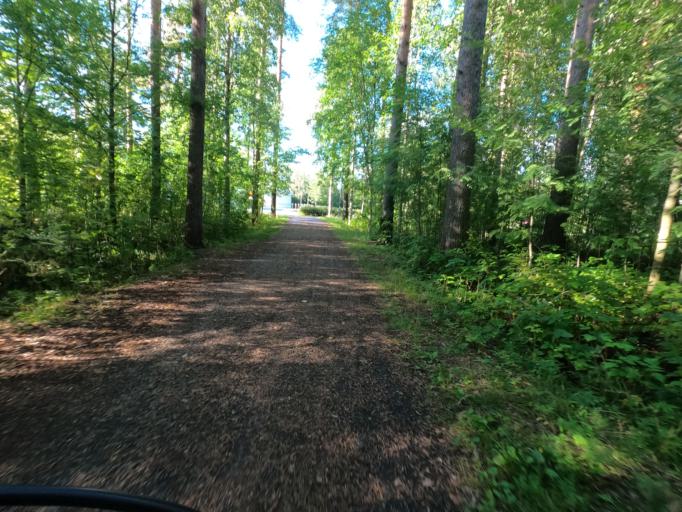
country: FI
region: North Karelia
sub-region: Joensuu
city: Joensuu
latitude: 62.6150
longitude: 29.7462
